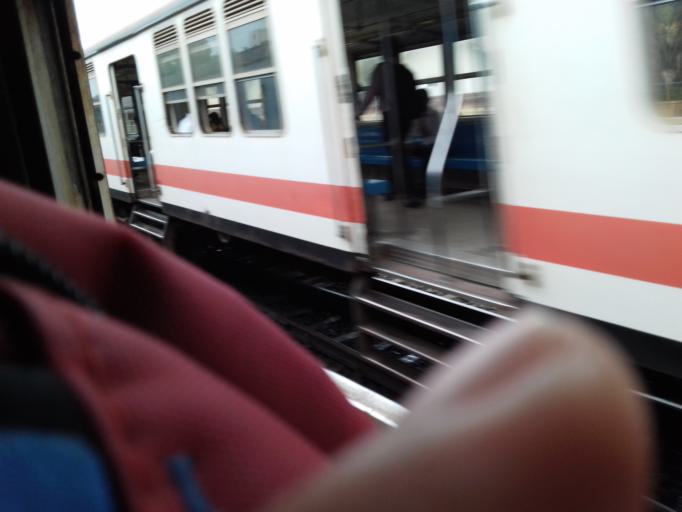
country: LK
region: Western
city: Colombo
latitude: 6.9329
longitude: 79.8533
